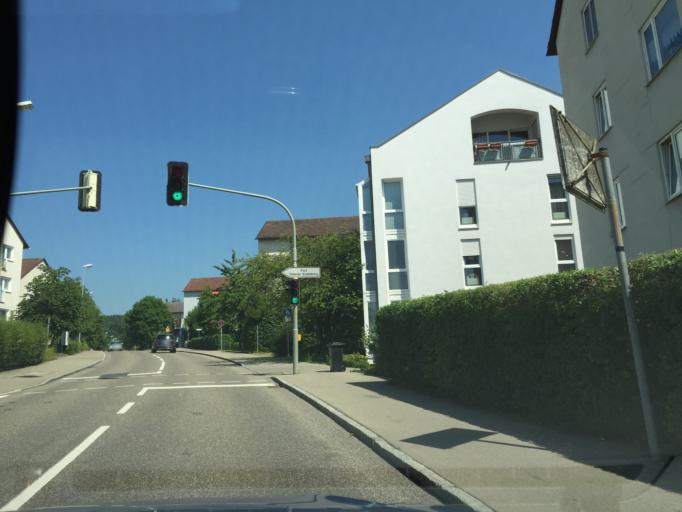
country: DE
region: Baden-Wuerttemberg
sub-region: Tuebingen Region
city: Ulm
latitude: 48.4107
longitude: 9.9659
